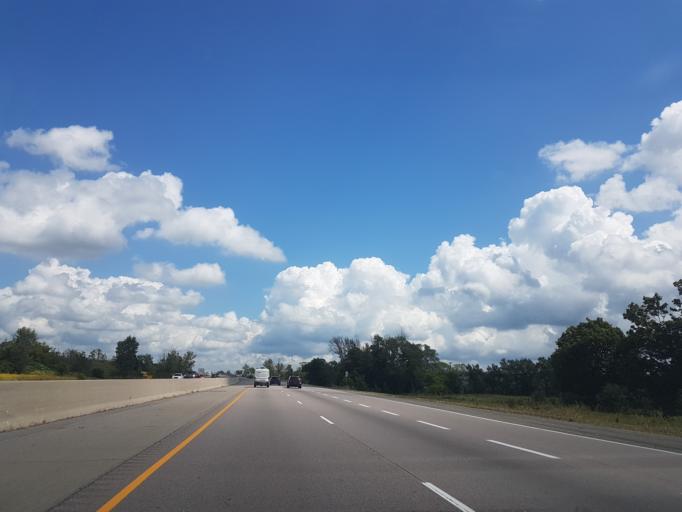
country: CA
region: Ontario
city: Belleville
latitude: 44.1952
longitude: -77.3865
